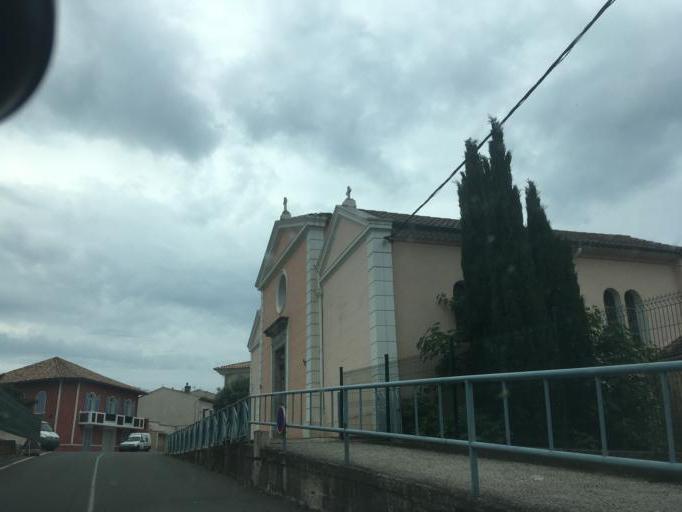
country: FR
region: Provence-Alpes-Cote d'Azur
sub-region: Departement du Var
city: La Londe-les-Maures
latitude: 43.1407
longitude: 6.2316
